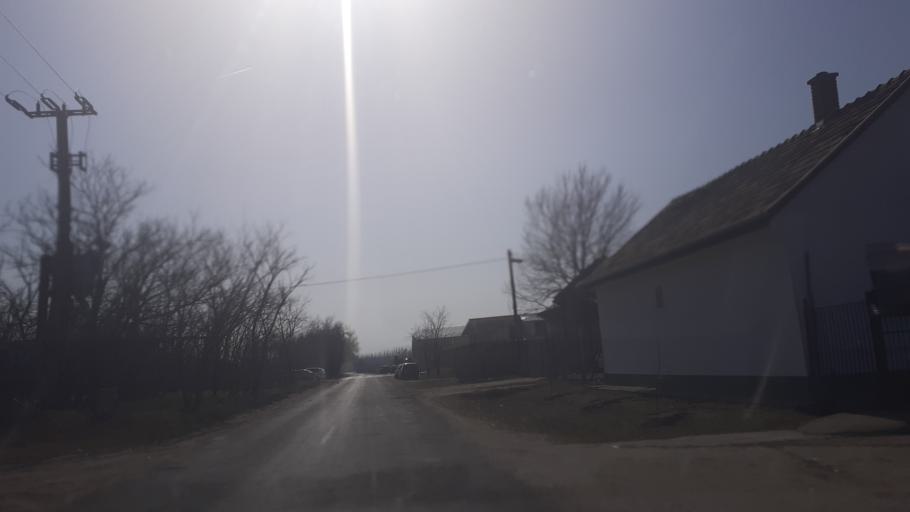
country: HU
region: Pest
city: Dabas
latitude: 47.1590
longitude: 19.3328
